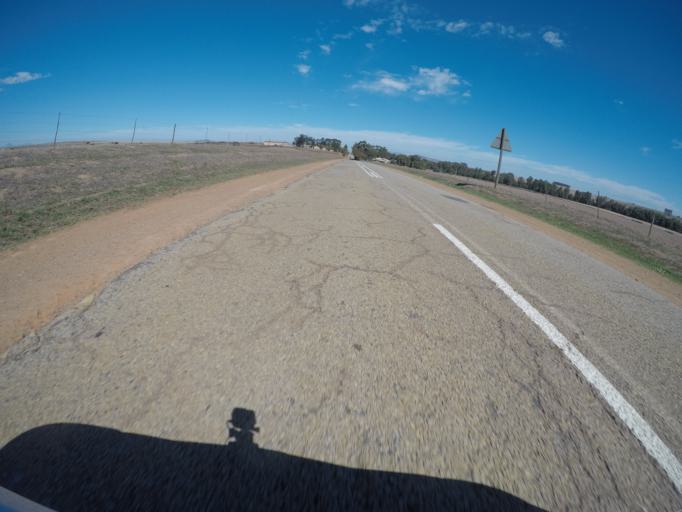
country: ZA
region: Western Cape
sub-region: City of Cape Town
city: Atlantis
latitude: -33.6077
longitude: 18.6385
